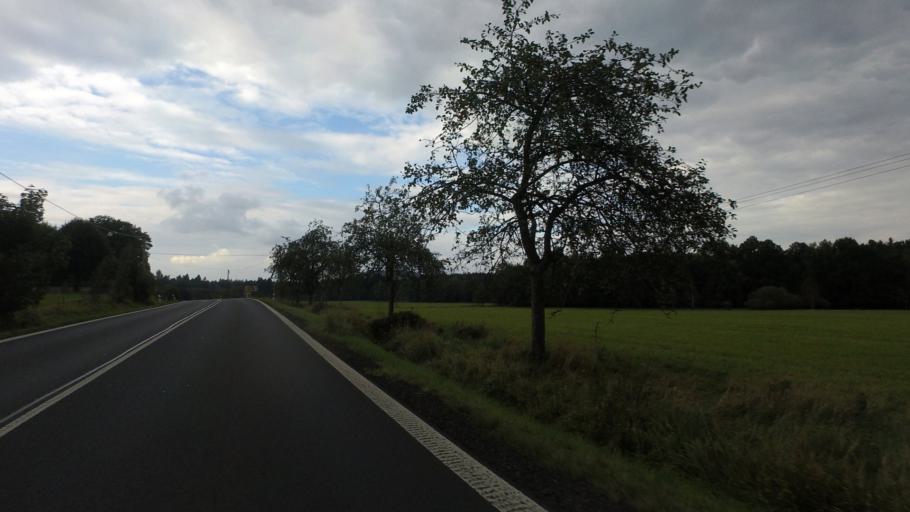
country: CZ
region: Ustecky
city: Stare Krecany
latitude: 50.9749
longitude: 14.5140
